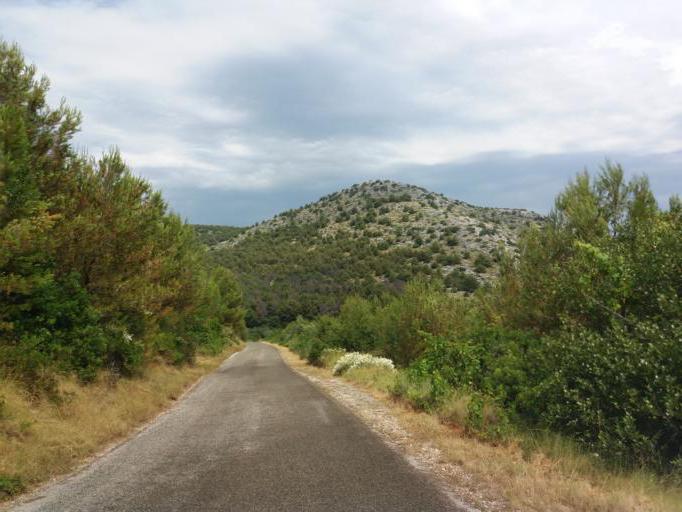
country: HR
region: Zadarska
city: Sali
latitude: 43.9195
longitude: 15.1296
